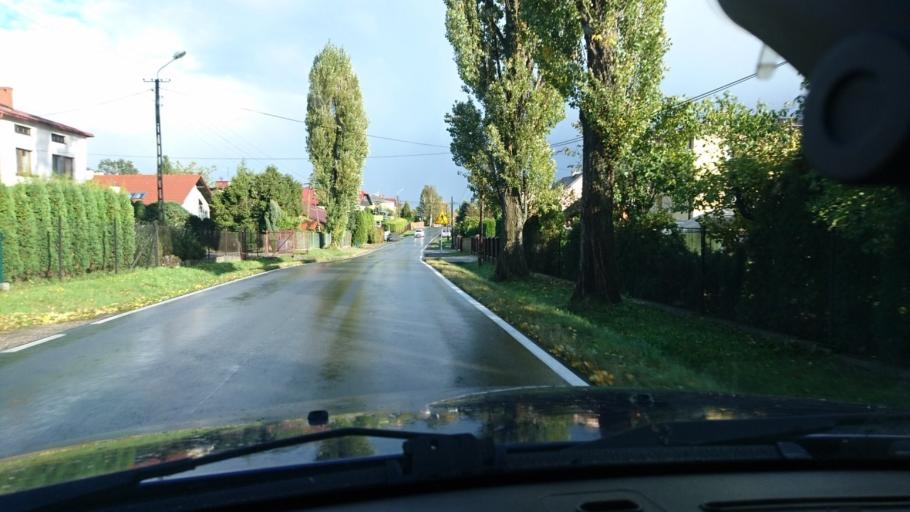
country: PL
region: Silesian Voivodeship
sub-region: Powiat bielski
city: Mazancowice
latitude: 49.8586
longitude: 19.0172
